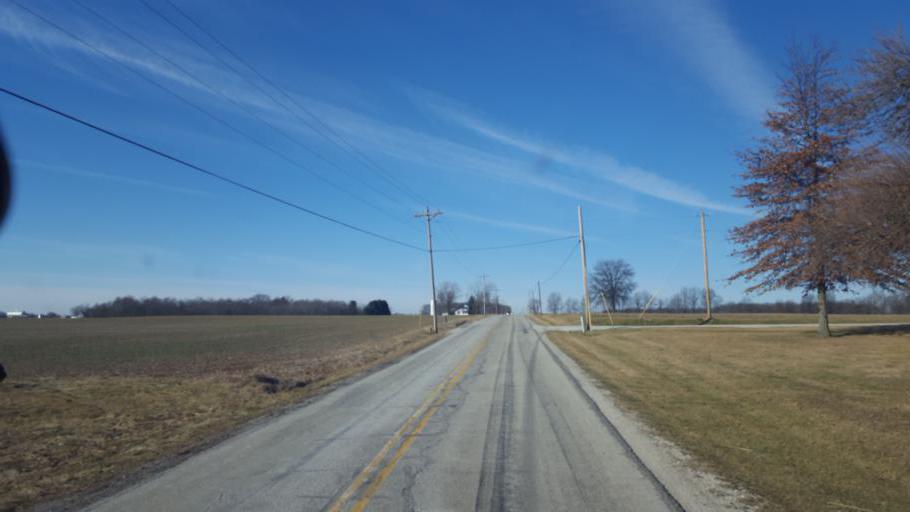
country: US
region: Ohio
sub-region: Morrow County
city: Cardington
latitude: 40.5279
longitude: -83.0149
